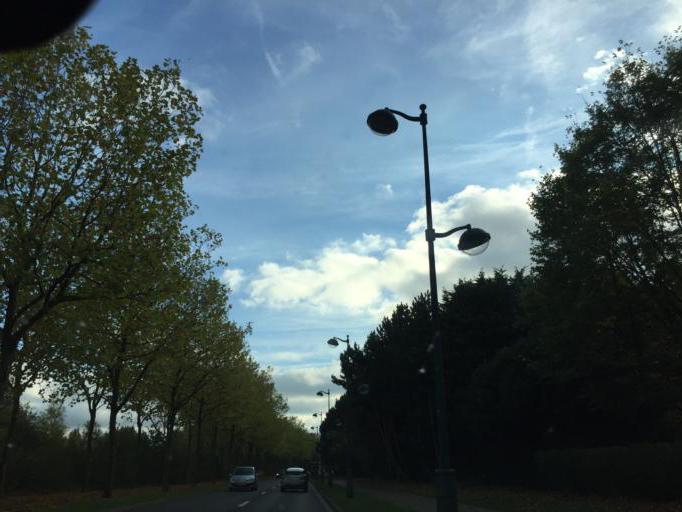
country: FR
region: Ile-de-France
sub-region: Departement de Seine-et-Marne
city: Serris
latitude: 48.8664
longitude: 2.7916
